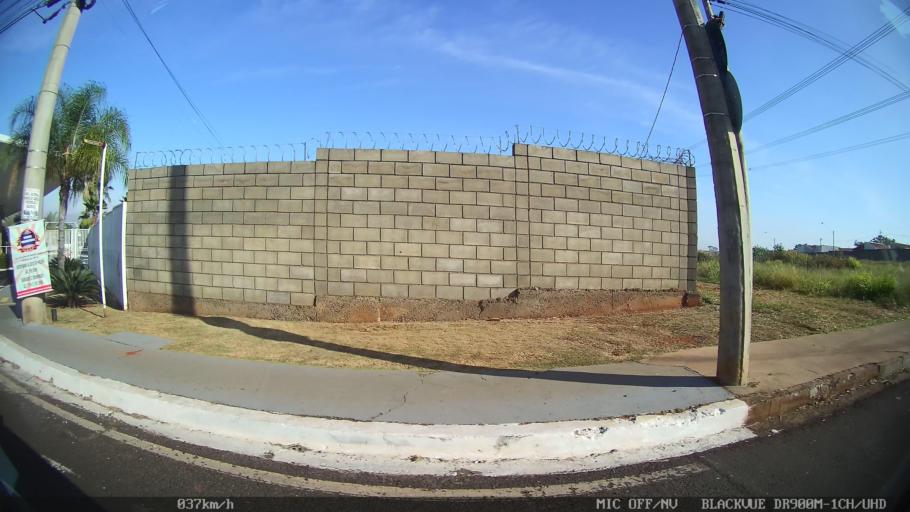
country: BR
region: Sao Paulo
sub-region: Sao Jose Do Rio Preto
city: Sao Jose do Rio Preto
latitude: -20.7682
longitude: -49.3304
